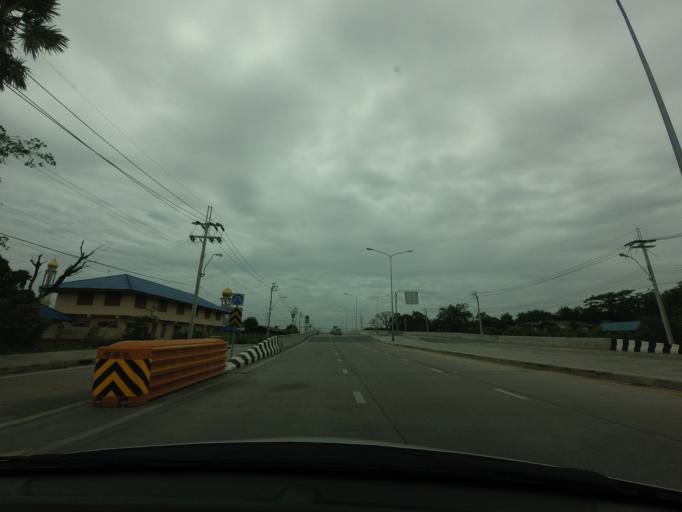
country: TH
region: Bangkok
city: Nong Chok
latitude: 13.8523
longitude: 100.8072
